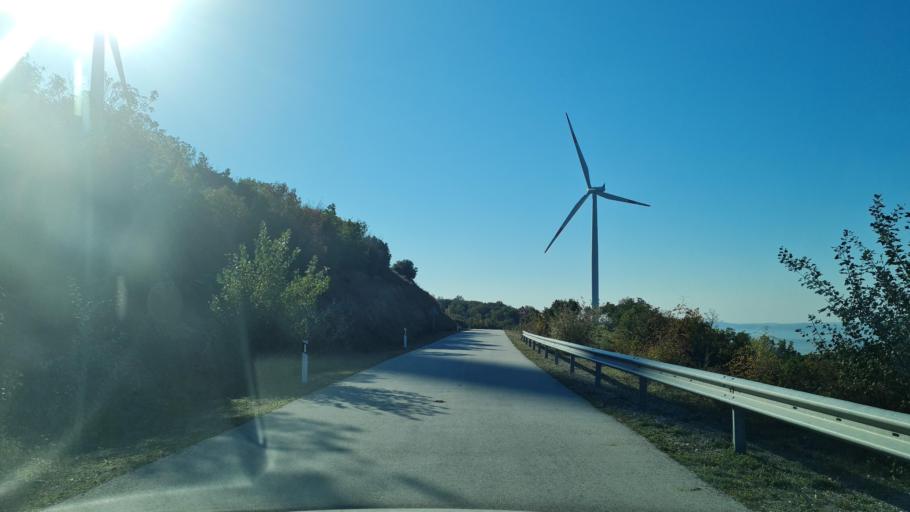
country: MK
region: Bogdanci
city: Bogdanci
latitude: 41.2260
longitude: 22.5531
